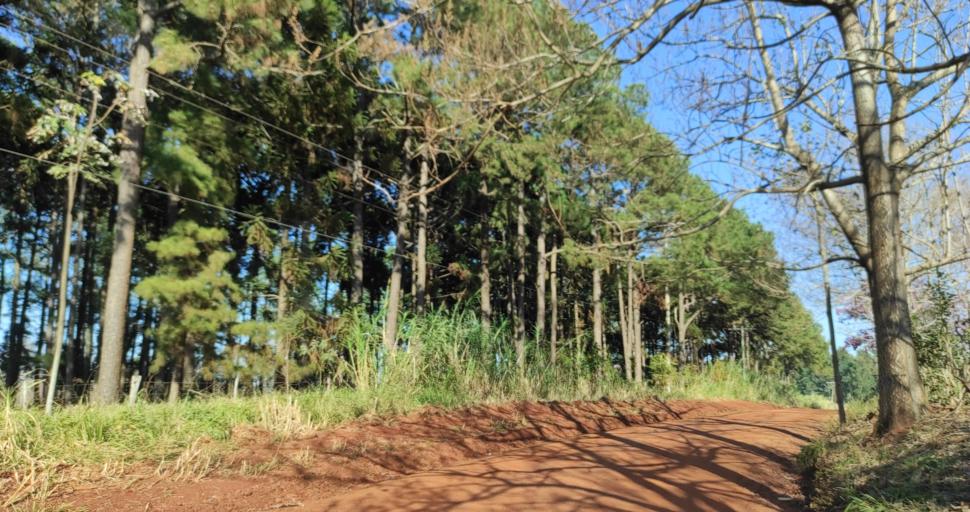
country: AR
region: Misiones
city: Puerto Rico
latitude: -26.8645
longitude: -55.0271
